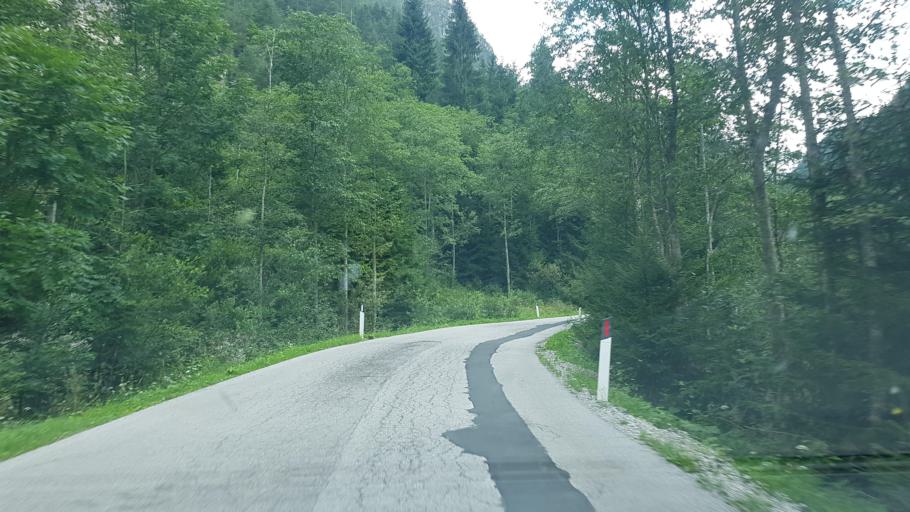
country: IT
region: Veneto
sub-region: Provincia di Belluno
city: San Pietro di Cadore
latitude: 46.5856
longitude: 12.6269
